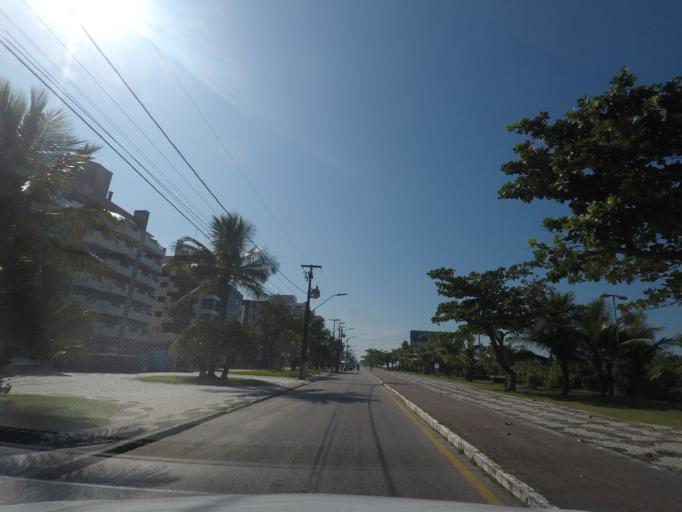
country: BR
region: Parana
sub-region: Guaratuba
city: Guaratuba
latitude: -25.8300
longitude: -48.5357
